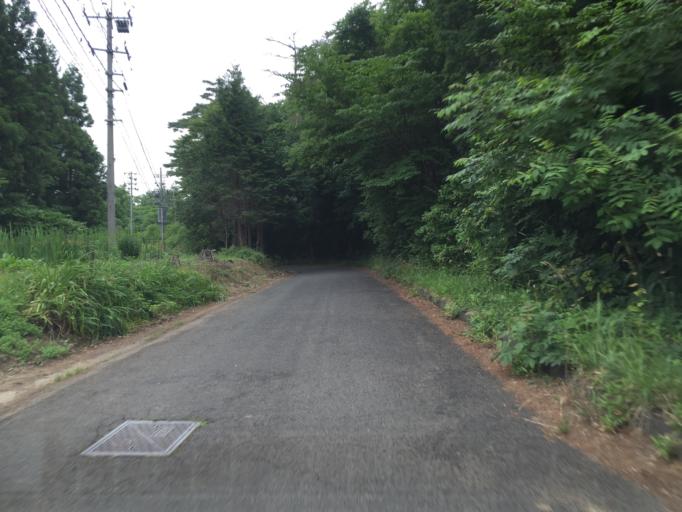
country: JP
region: Fukushima
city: Fukushima-shi
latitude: 37.7125
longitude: 140.4649
